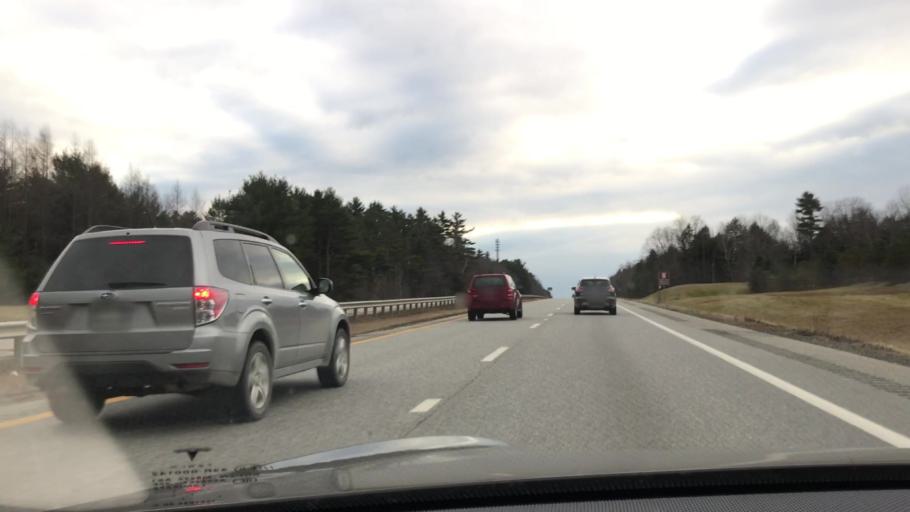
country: US
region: Maine
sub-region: Kennebec County
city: Hallowell
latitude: 44.2735
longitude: -69.8065
